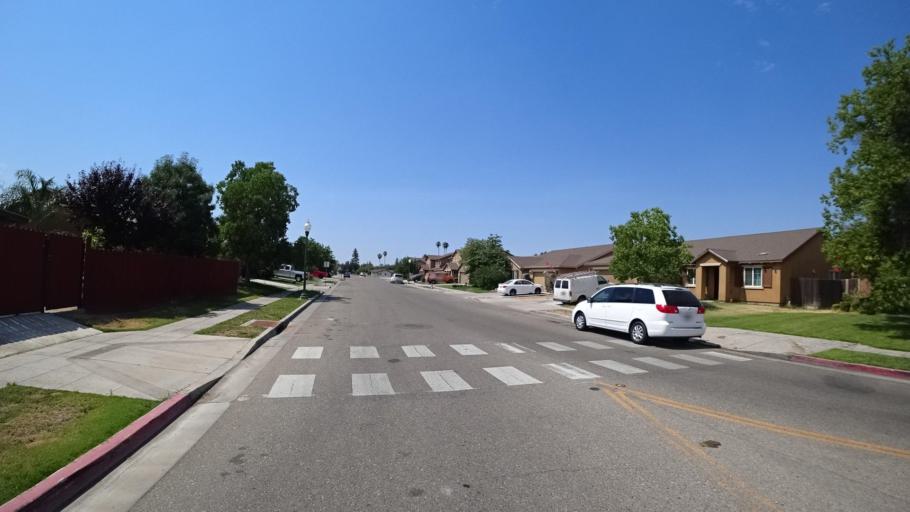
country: US
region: California
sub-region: Fresno County
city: Sunnyside
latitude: 36.7380
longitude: -119.6895
